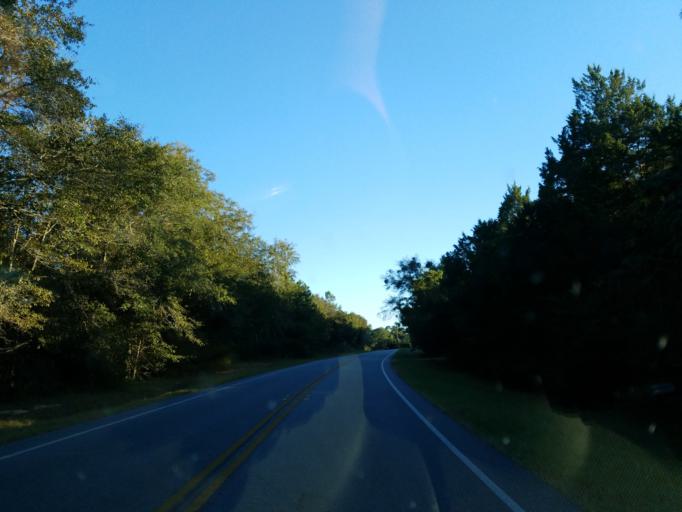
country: US
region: Georgia
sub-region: Worth County
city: Sylvester
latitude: 31.5764
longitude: -83.8550
